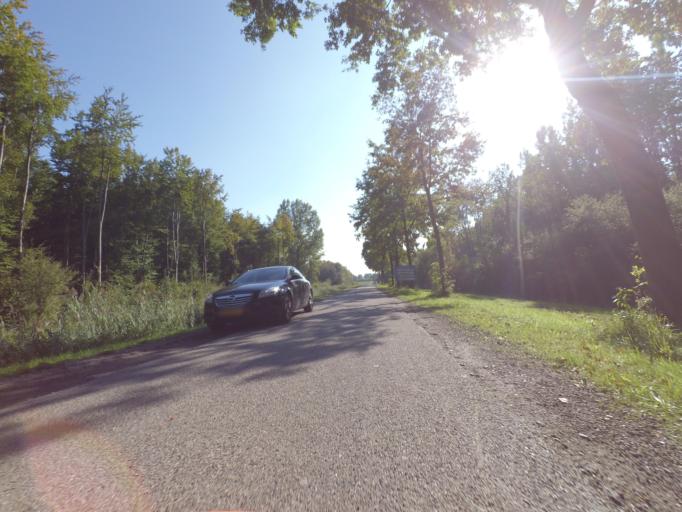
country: NL
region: Flevoland
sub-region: Gemeente Zeewolde
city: Zeewolde
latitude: 52.2776
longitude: 5.5193
